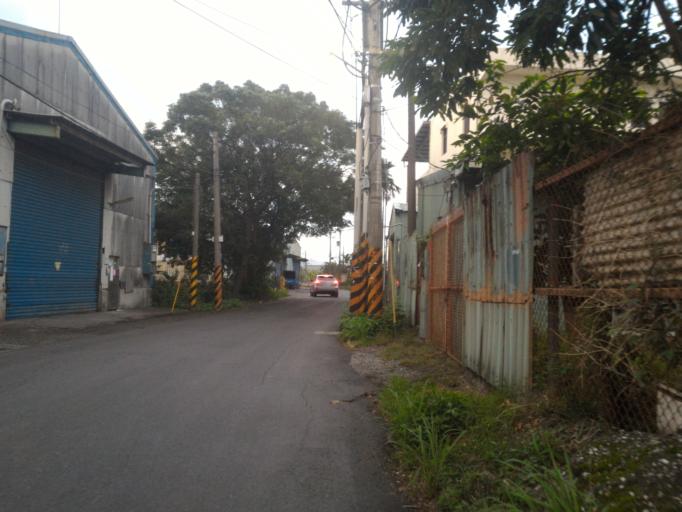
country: TW
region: Taipei
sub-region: Taipei
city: Banqiao
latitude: 24.9503
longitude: 121.4018
